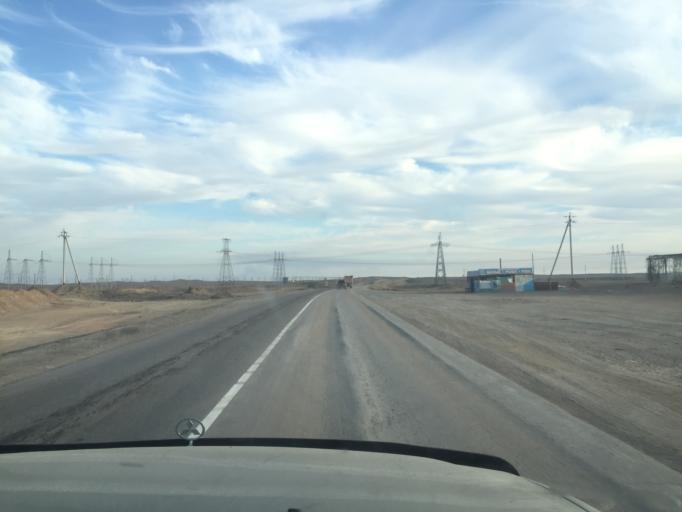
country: KZ
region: Almaty Oblysy
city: Ulken
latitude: 45.1931
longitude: 73.9100
